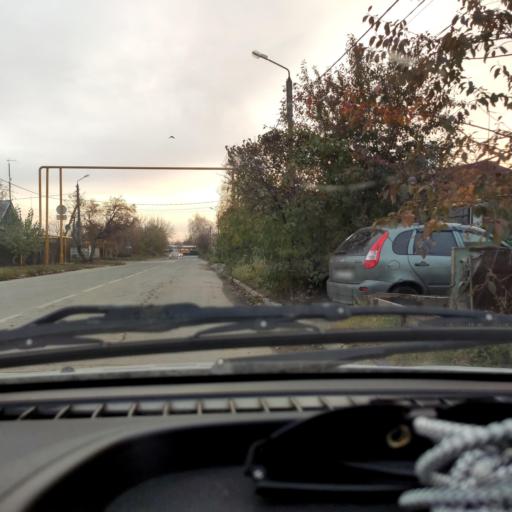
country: RU
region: Samara
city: Tol'yatti
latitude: 53.5369
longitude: 49.4249
